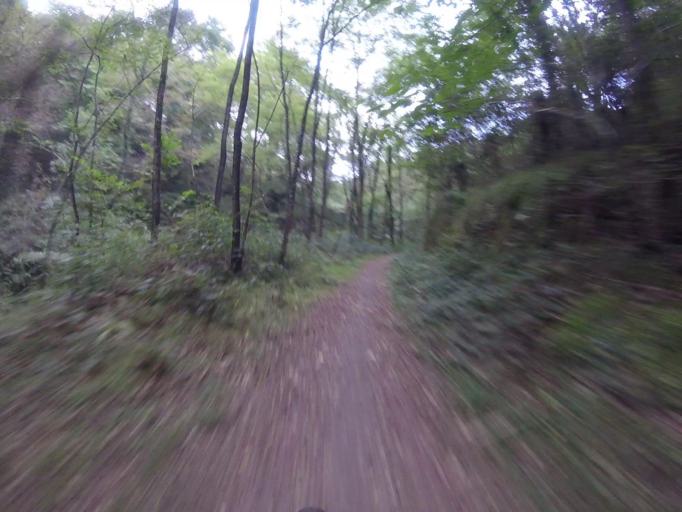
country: ES
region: Basque Country
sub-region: Provincia de Guipuzcoa
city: Errenteria
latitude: 43.2724
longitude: -1.8409
